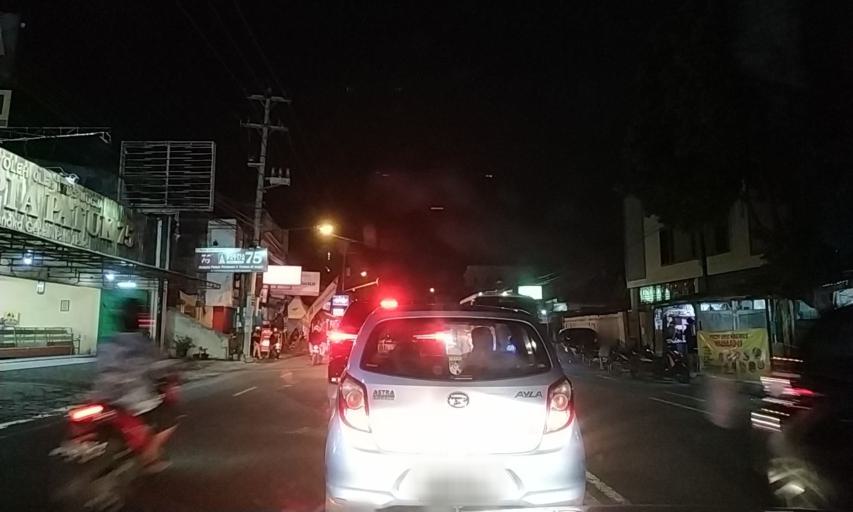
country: ID
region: Daerah Istimewa Yogyakarta
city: Yogyakarta
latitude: -7.7938
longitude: 110.3532
